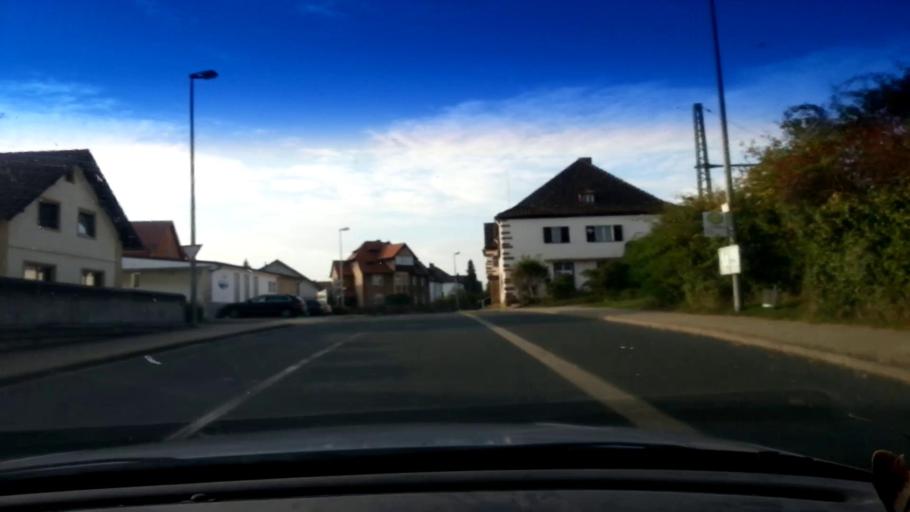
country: DE
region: Bavaria
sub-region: Upper Franconia
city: Hirschaid
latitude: 49.8190
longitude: 10.9913
